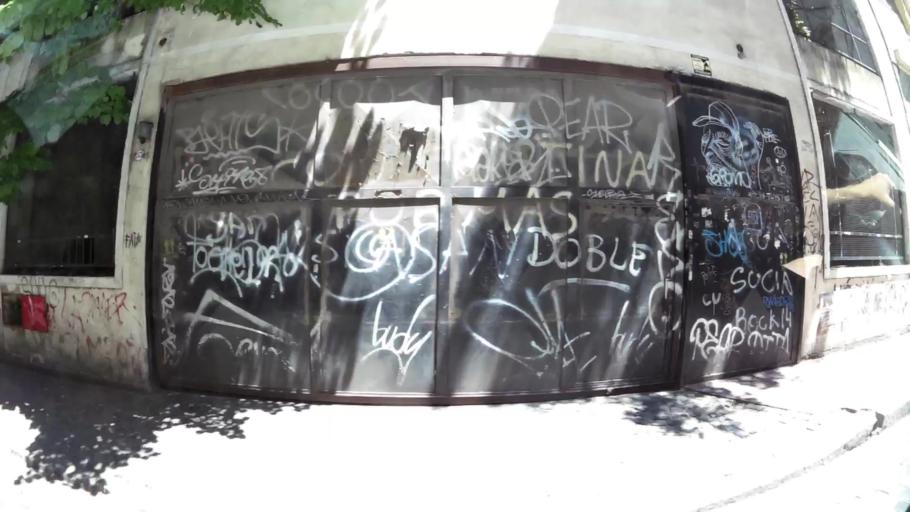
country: AR
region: Buenos Aires F.D.
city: Buenos Aires
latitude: -34.6109
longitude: -58.3720
